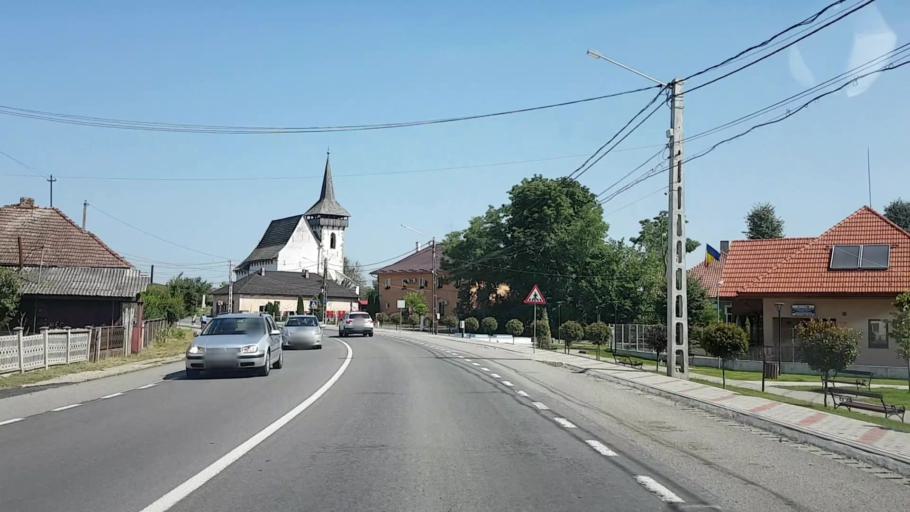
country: RO
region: Bistrita-Nasaud
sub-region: Comuna Sintereag
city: Sintereag
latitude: 47.1806
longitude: 24.2868
